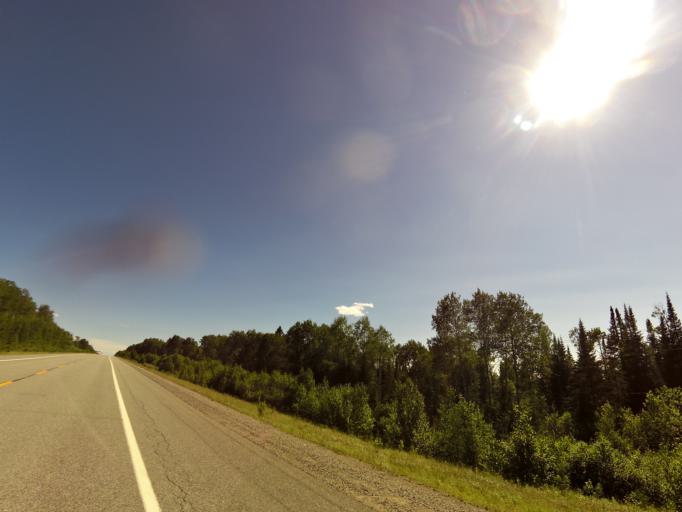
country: CA
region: Quebec
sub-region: Abitibi-Temiscamingue
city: Senneterre
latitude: 48.0102
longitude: -77.3607
